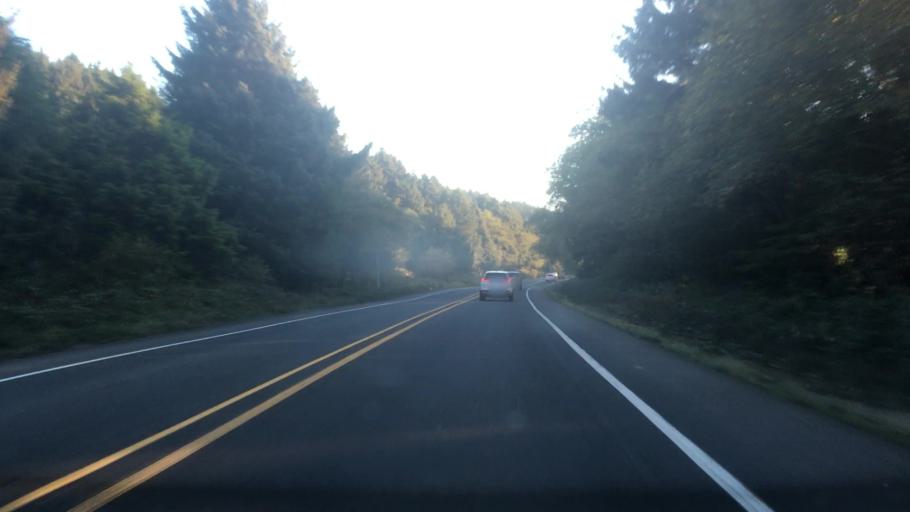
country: US
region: Oregon
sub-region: Clatsop County
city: Cannon Beach
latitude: 45.8649
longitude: -123.9590
